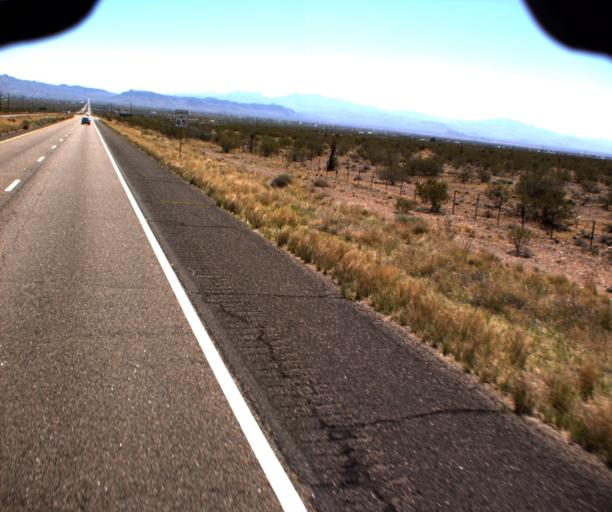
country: US
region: Arizona
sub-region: Mohave County
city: Golden Valley
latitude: 35.2266
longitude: -114.3123
